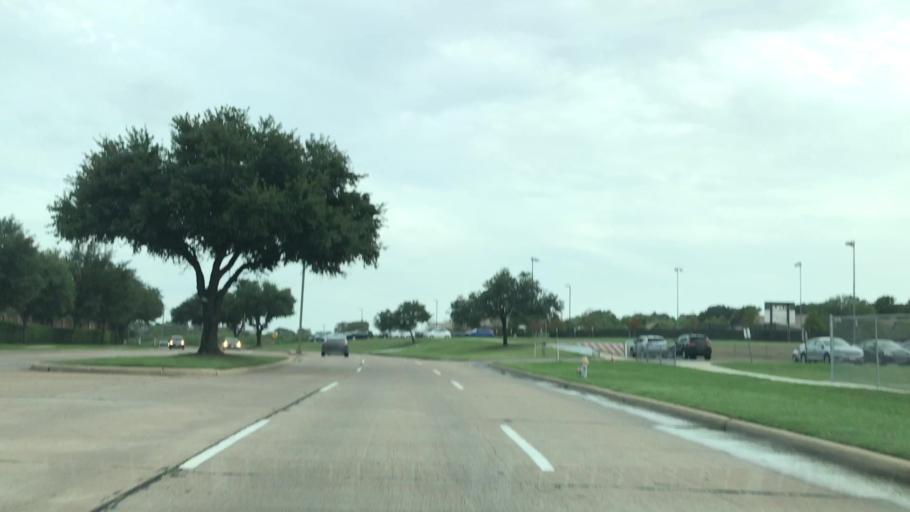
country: US
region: Texas
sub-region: Dallas County
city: Irving
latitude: 32.8637
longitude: -96.9773
